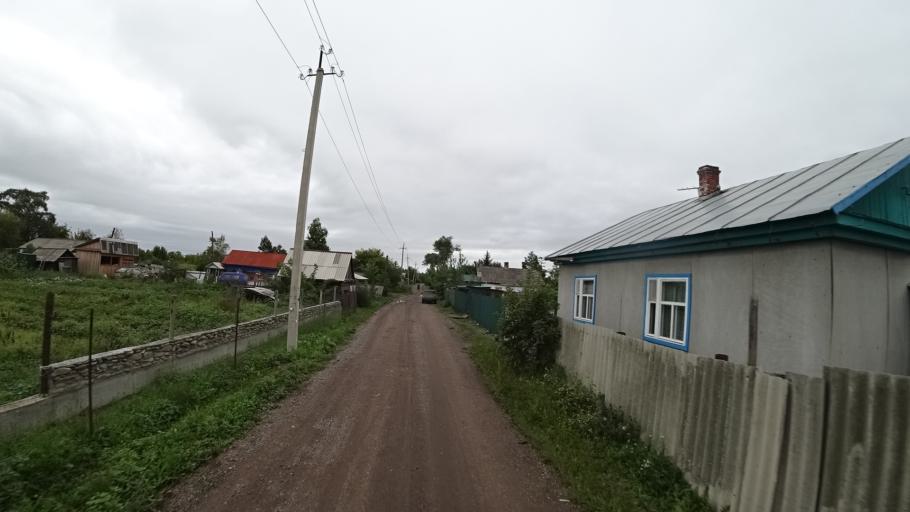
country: RU
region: Primorskiy
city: Chernigovka
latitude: 44.3374
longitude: 132.5362
